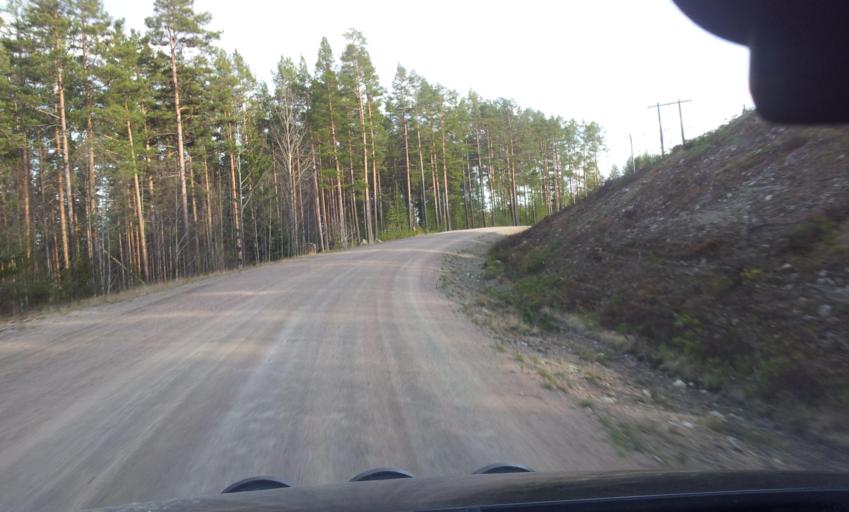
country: SE
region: Vaesternorrland
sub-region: Ange Kommun
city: Ange
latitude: 62.1657
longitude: 15.6579
